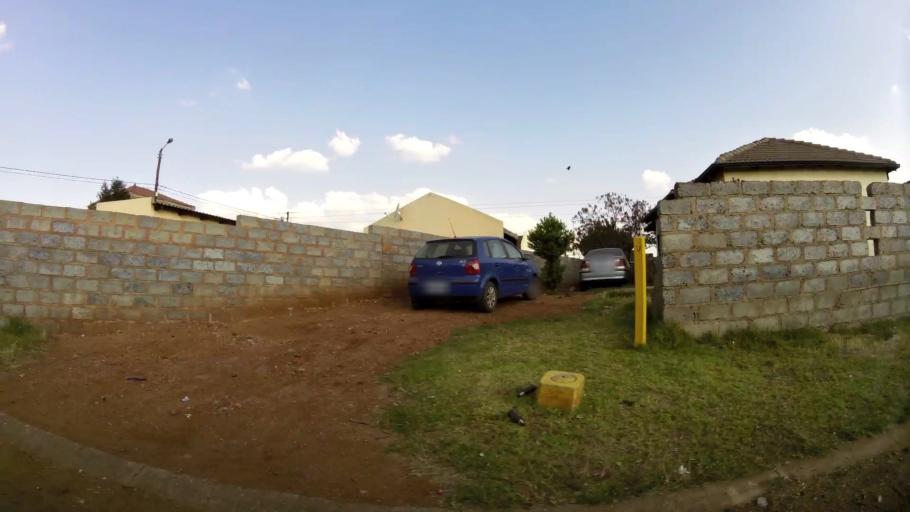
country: ZA
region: Gauteng
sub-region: Ekurhuleni Metropolitan Municipality
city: Tembisa
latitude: -25.9514
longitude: 28.2112
